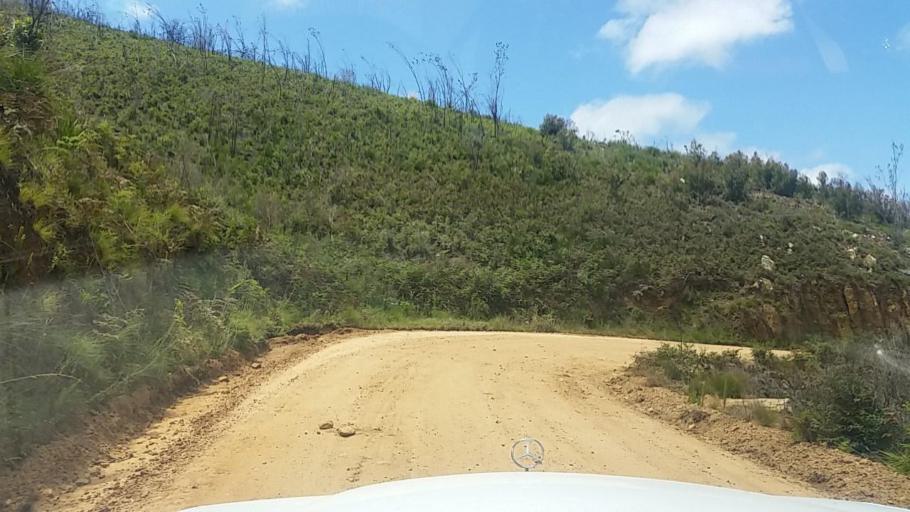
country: ZA
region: Western Cape
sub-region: Eden District Municipality
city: Knysna
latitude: -33.8796
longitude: 23.1554
